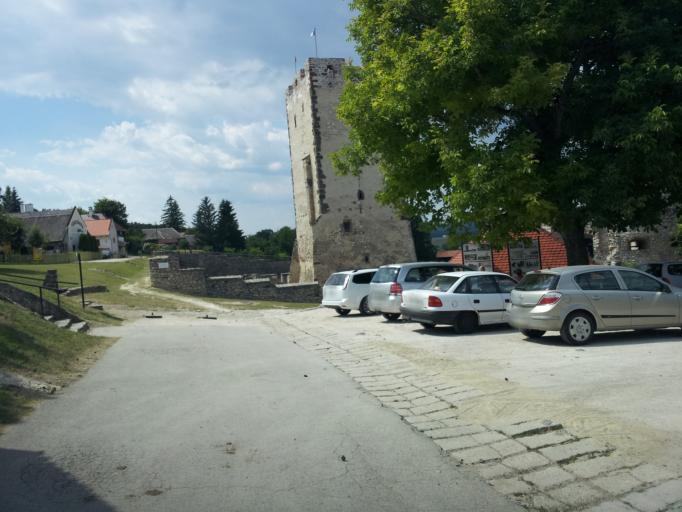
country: HU
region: Veszprem
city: Urkut
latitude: 46.9846
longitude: 17.6964
